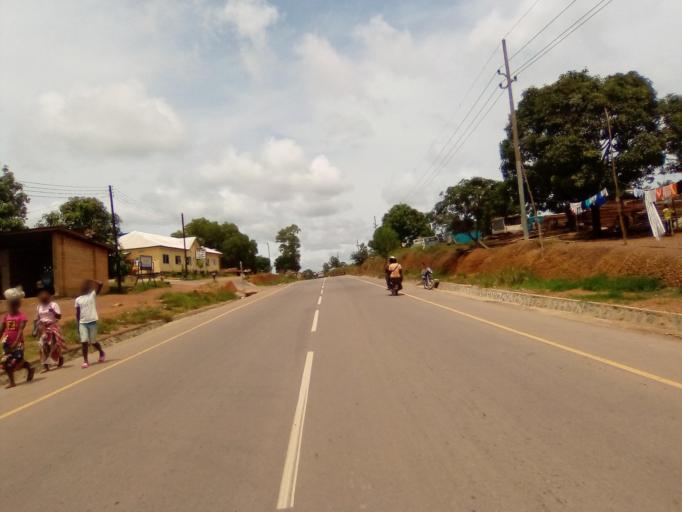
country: SL
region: Southern Province
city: Bo
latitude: 7.9331
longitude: -11.7251
